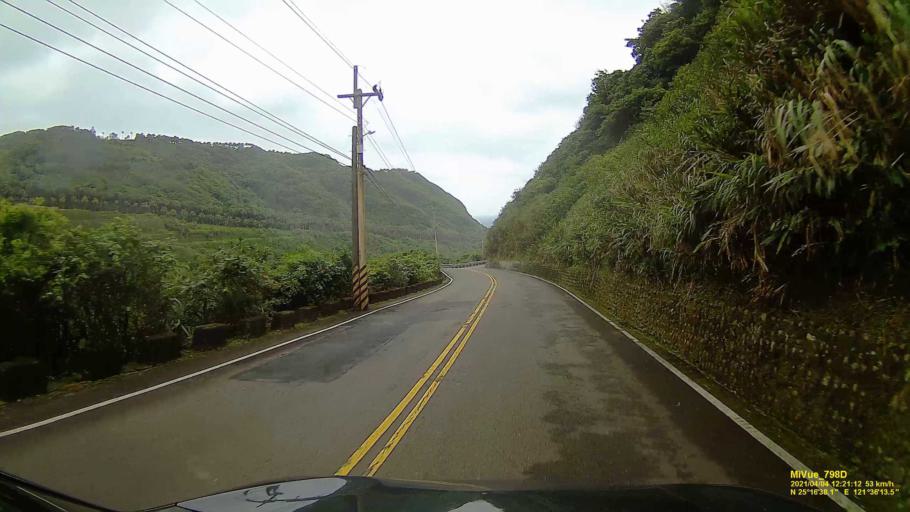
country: TW
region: Taiwan
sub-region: Keelung
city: Keelung
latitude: 25.2776
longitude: 121.6039
